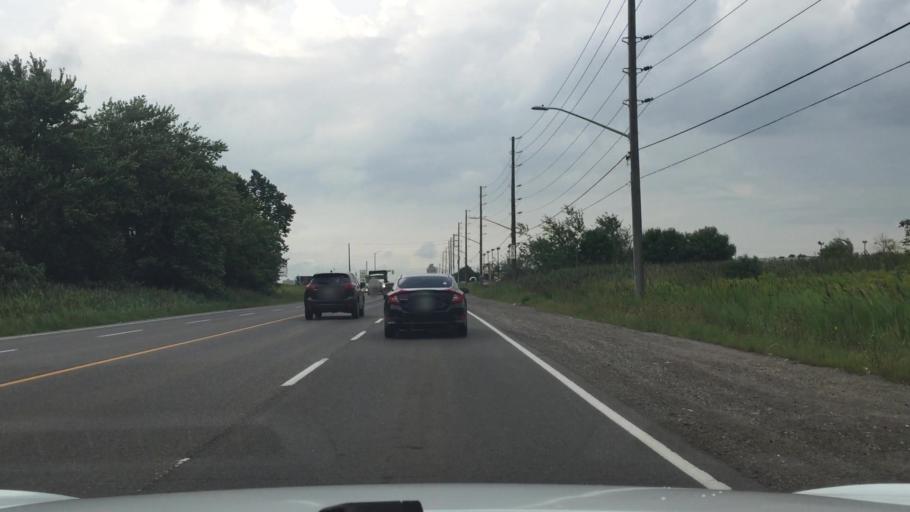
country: CA
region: Ontario
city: Ajax
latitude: 43.8371
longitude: -79.0537
